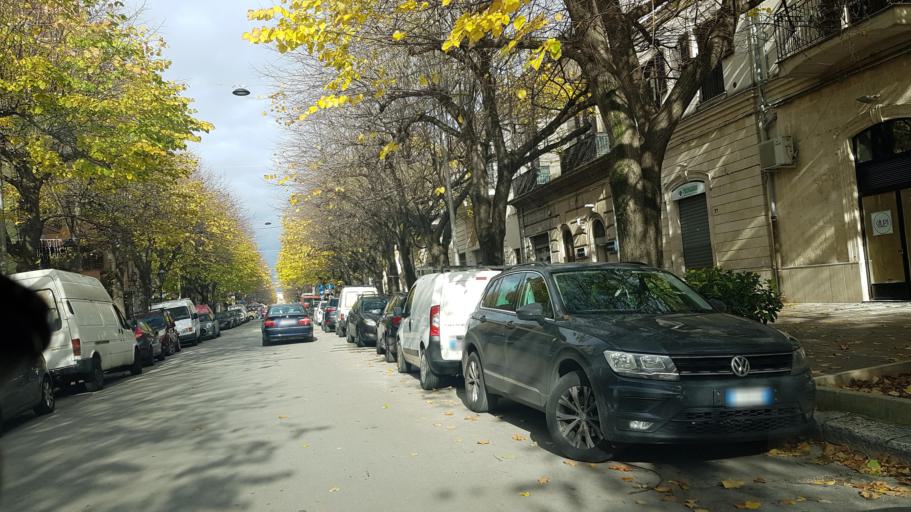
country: IT
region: Apulia
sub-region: Provincia di Brindisi
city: Francavilla Fontana
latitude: 40.5238
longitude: 17.5846
